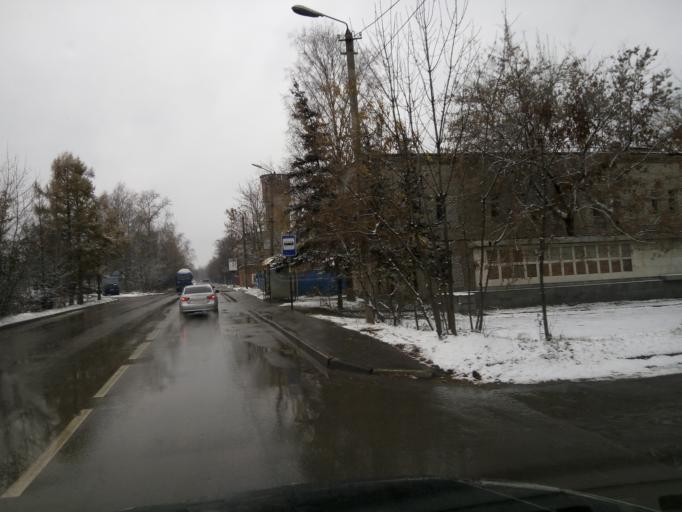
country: RU
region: Moskovskaya
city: Skhodnya
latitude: 55.9441
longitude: 37.2822
